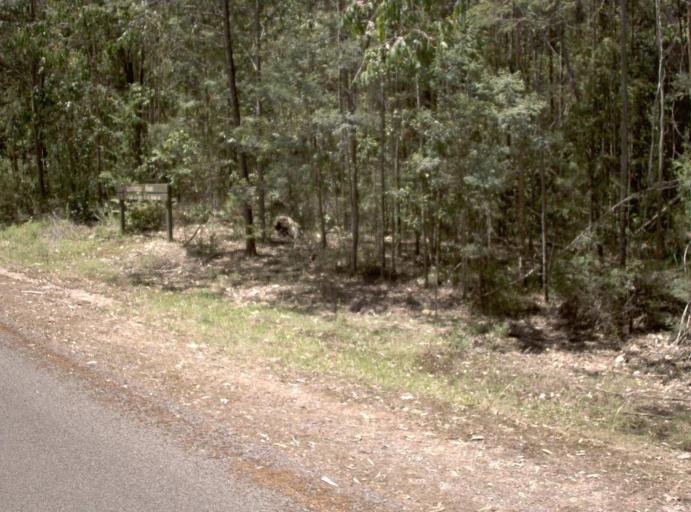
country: AU
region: New South Wales
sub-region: Bombala
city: Bombala
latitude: -37.4452
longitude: 148.9360
